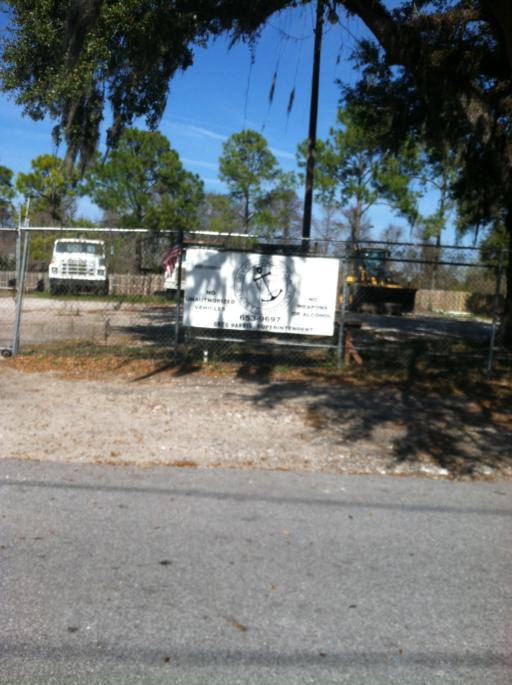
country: US
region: Florida
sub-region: Franklin County
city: Apalachicola
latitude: 29.7306
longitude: -84.9915
